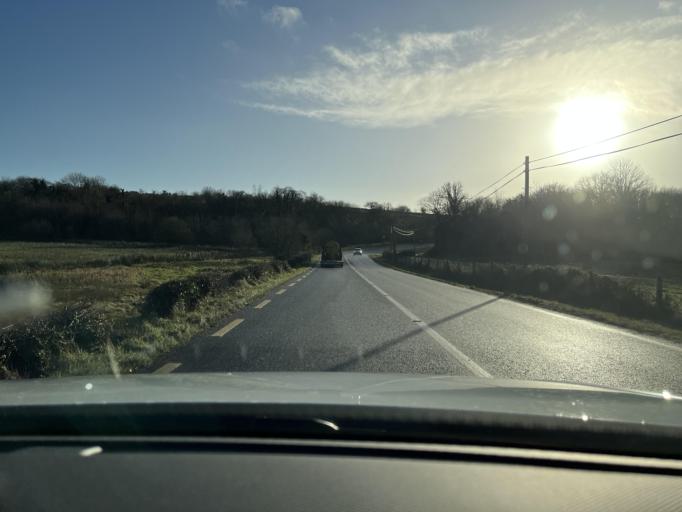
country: IE
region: Connaught
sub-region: County Leitrim
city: Manorhamilton
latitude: 54.2253
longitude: -8.2042
